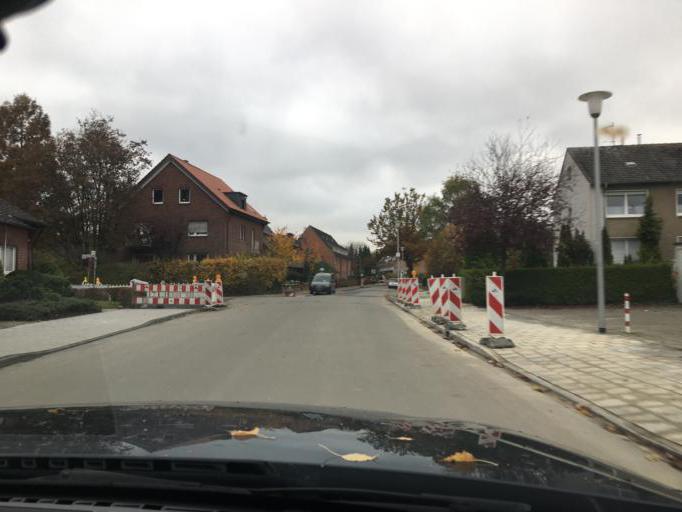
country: DE
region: North Rhine-Westphalia
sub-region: Regierungsbezirk Munster
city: Muenster
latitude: 51.9805
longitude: 7.6472
